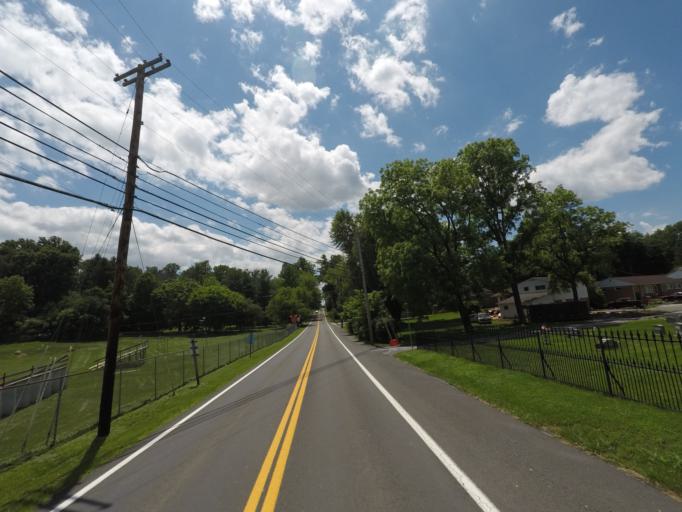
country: US
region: West Virginia
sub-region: Jefferson County
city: Shepherdstown
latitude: 39.4279
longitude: -77.8127
